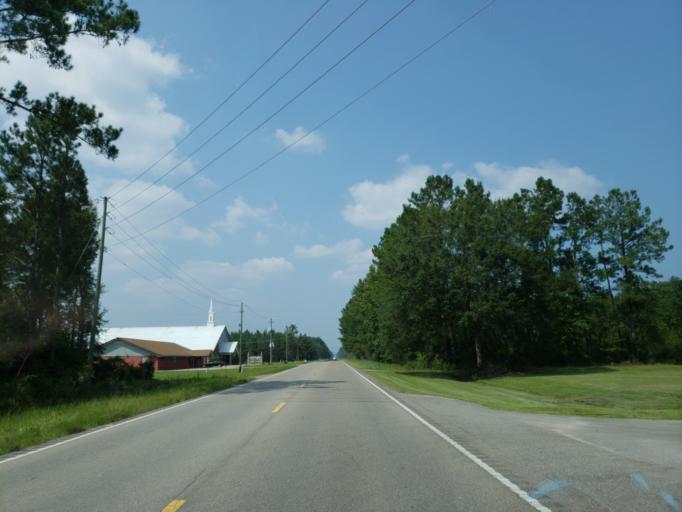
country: US
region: Mississippi
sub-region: Forrest County
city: Glendale
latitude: 31.4534
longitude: -89.2856
